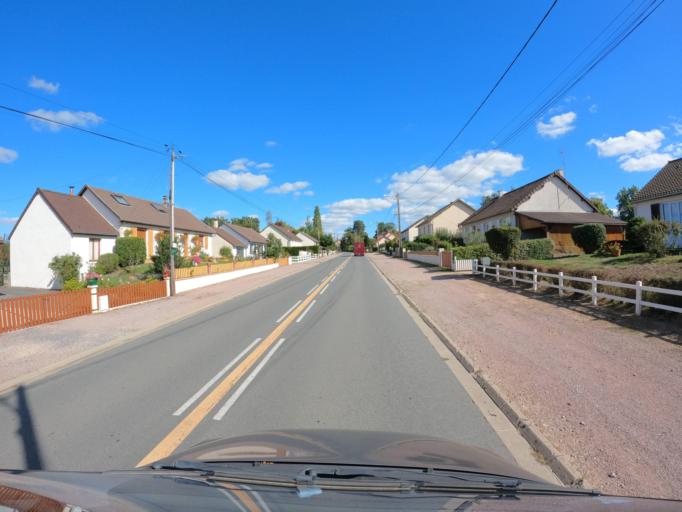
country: FR
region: Auvergne
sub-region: Departement de l'Allier
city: Doyet
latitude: 46.3973
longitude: 2.8506
